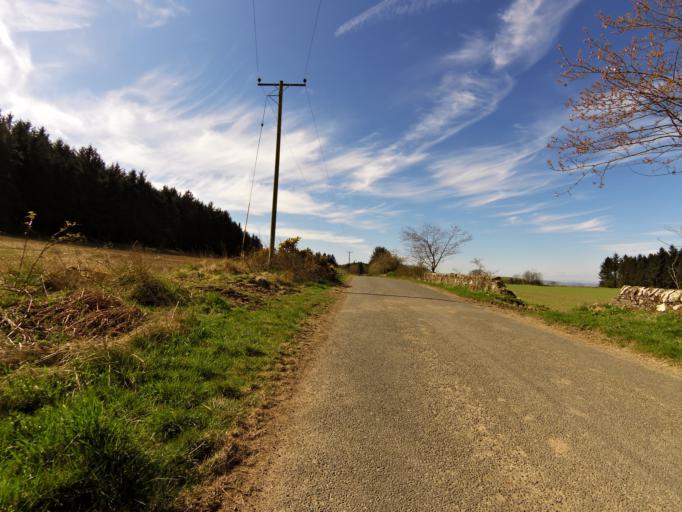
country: GB
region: Scotland
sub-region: Fife
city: Cupar
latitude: 56.3891
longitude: -3.0681
